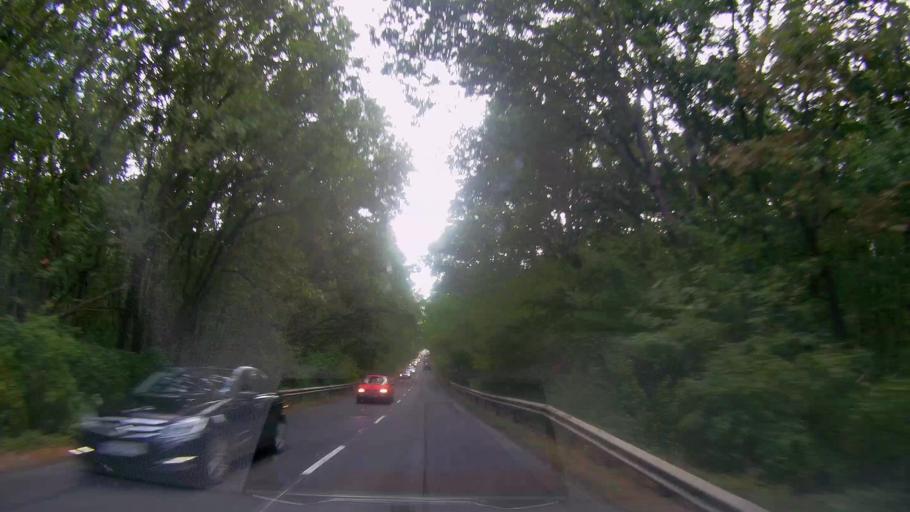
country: BG
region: Burgas
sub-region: Obshtina Primorsko
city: Primorsko
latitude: 42.2815
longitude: 27.7381
